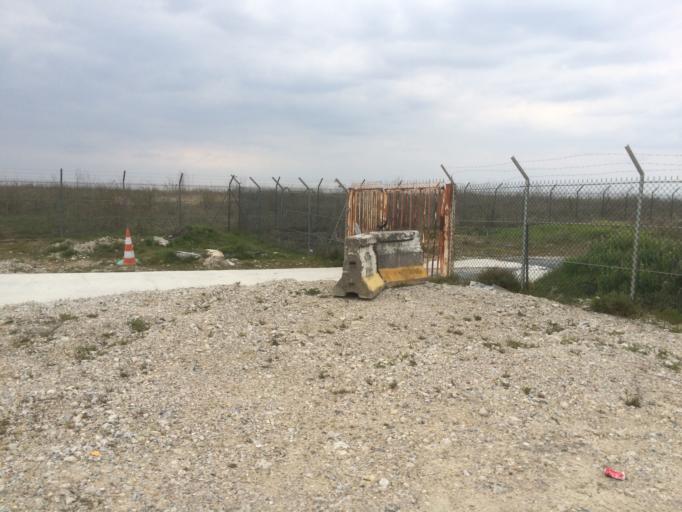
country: FR
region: Ile-de-France
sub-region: Departement de l'Essonne
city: Paray-Vieille-Poste
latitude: 48.7257
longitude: 2.3472
